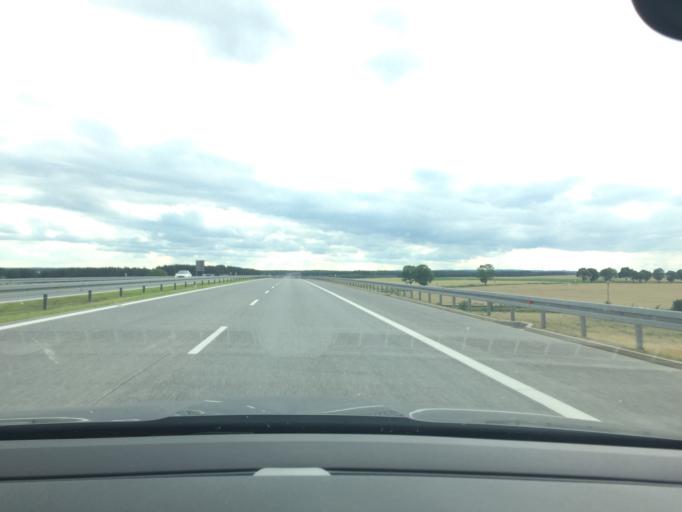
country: PL
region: Lubusz
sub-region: Powiat swiebodzinski
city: Zbaszynek
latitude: 52.3099
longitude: 15.7719
